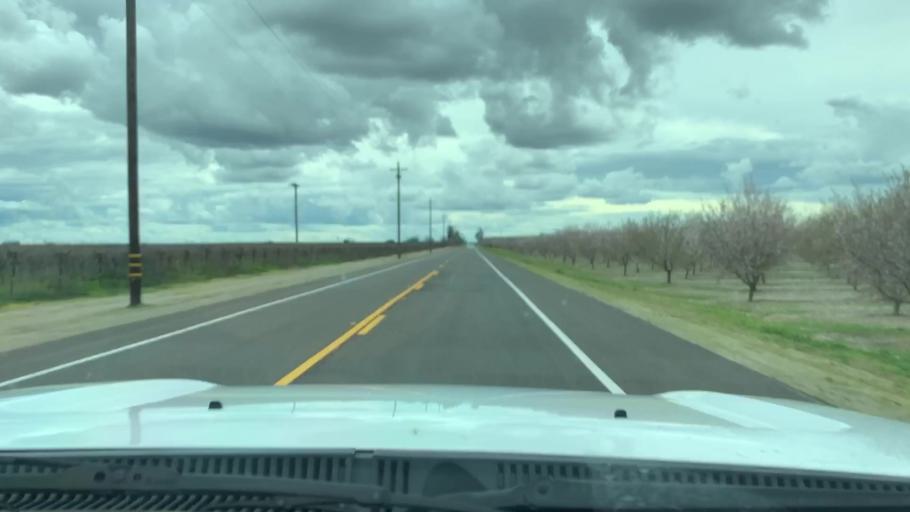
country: US
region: California
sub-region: Fresno County
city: Selma
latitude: 36.5248
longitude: -119.6829
